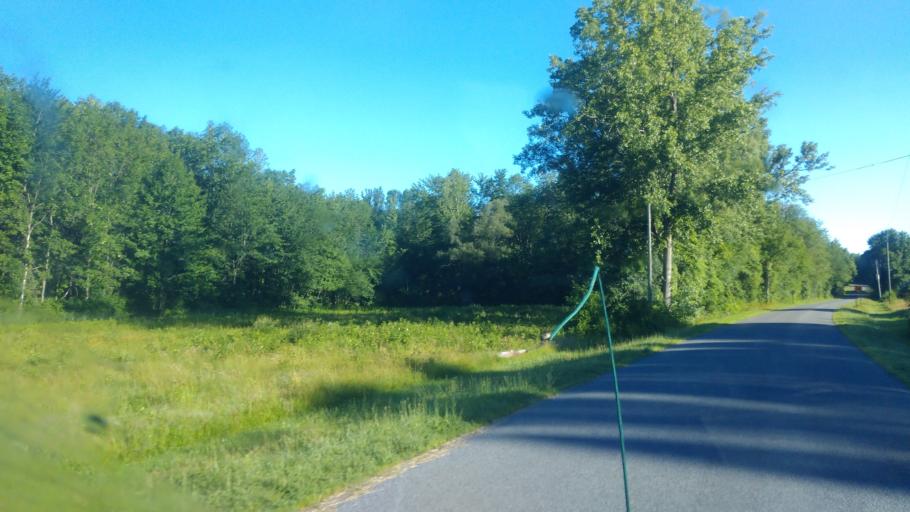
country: US
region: New York
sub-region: Wayne County
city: Sodus
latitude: 43.1451
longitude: -77.0430
